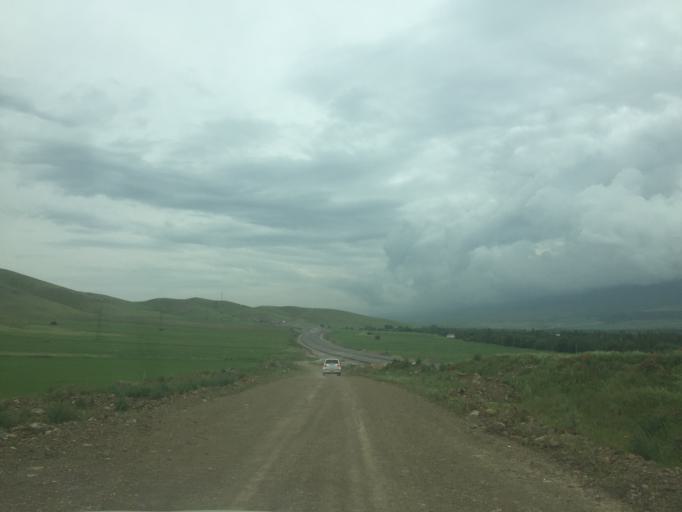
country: KZ
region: Ongtustik Qazaqstan
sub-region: Tulkibas Audany
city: Zhabagly
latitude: 42.5182
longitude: 70.5425
